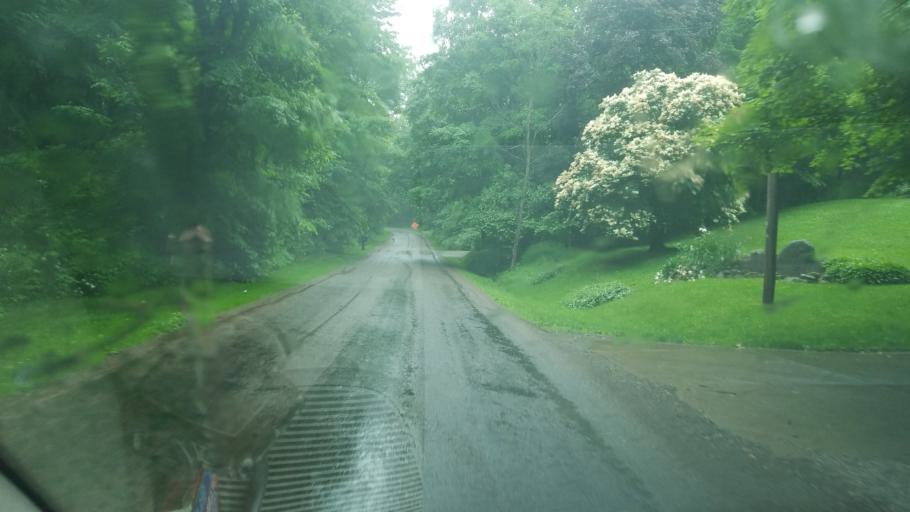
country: US
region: Ohio
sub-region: Sandusky County
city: Bellville
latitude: 40.6100
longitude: -82.4352
